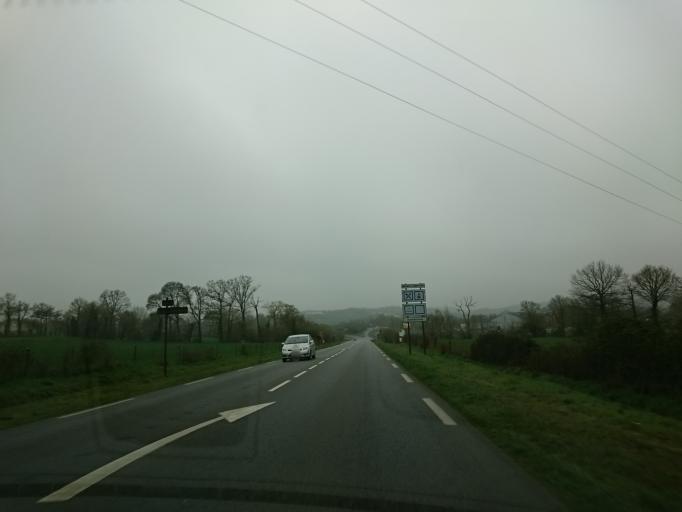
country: FR
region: Brittany
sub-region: Departement d'Ille-et-Vilaine
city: Bourg-des-Comptes
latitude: 47.9286
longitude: -1.7268
